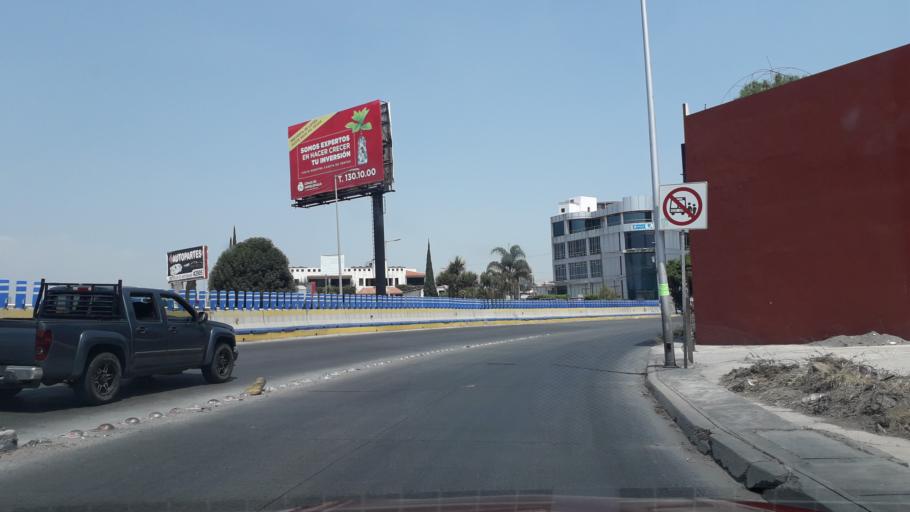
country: MX
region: Puebla
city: Puebla
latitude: 19.0496
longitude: -98.2382
